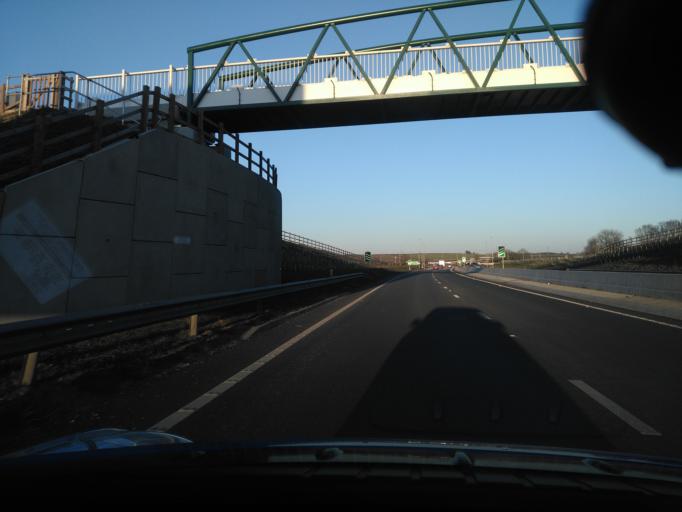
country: GB
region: England
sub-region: Central Bedfordshire
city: Houghton Regis
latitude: 51.9181
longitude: -0.5381
